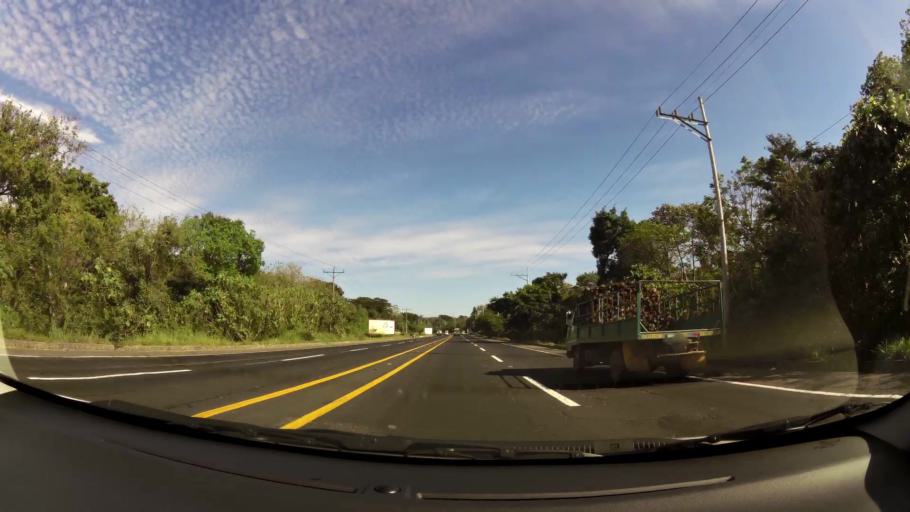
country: SV
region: Santa Ana
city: Santa Ana
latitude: 13.9868
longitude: -89.6054
